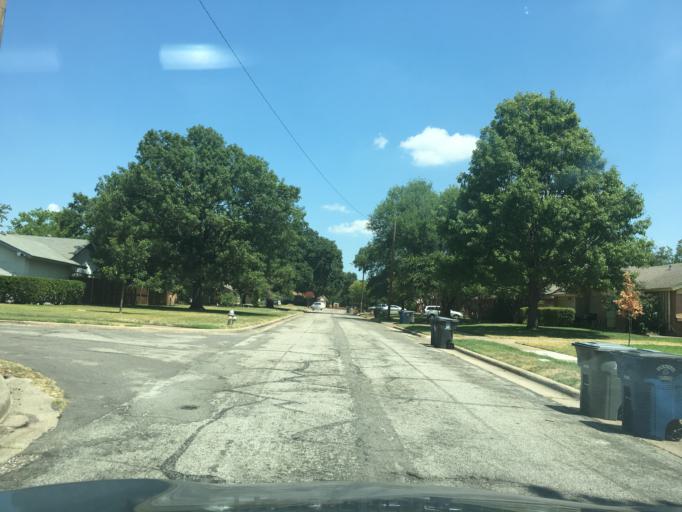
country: US
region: Texas
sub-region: Dallas County
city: Garland
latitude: 32.8660
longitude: -96.6896
